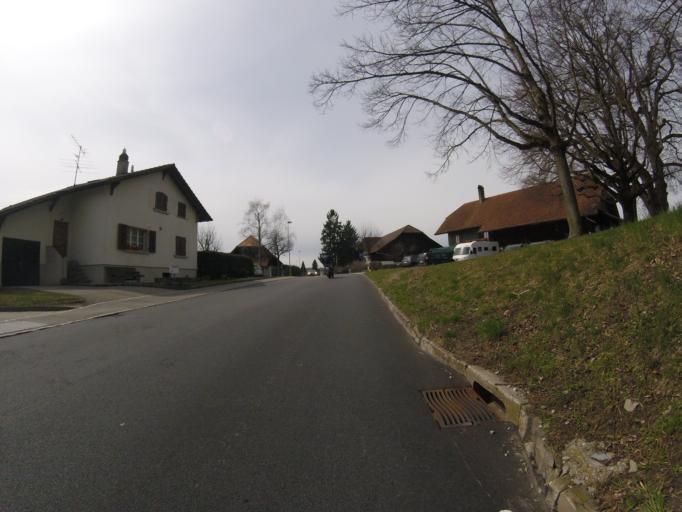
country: CH
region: Fribourg
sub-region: Sense District
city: Dudingen
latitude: 46.8946
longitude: 7.1785
